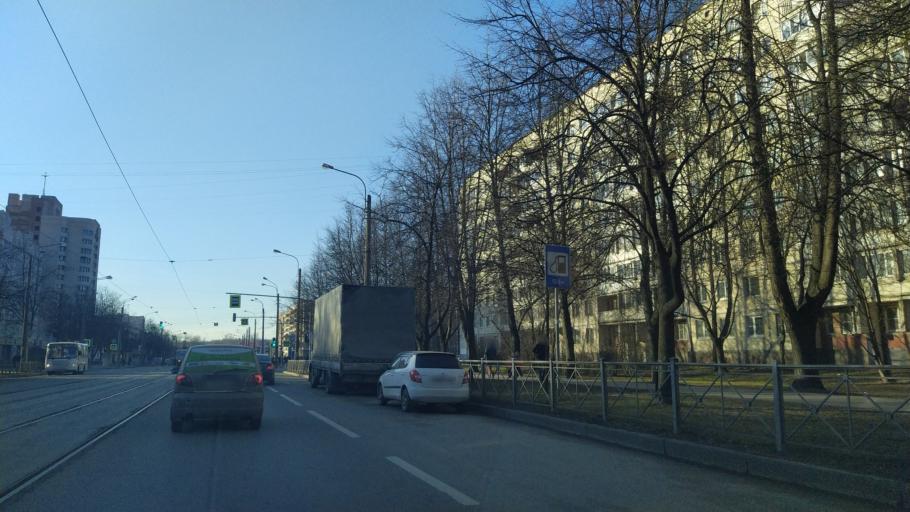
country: RU
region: Leningrad
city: Akademicheskoe
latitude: 60.0162
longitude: 30.3834
